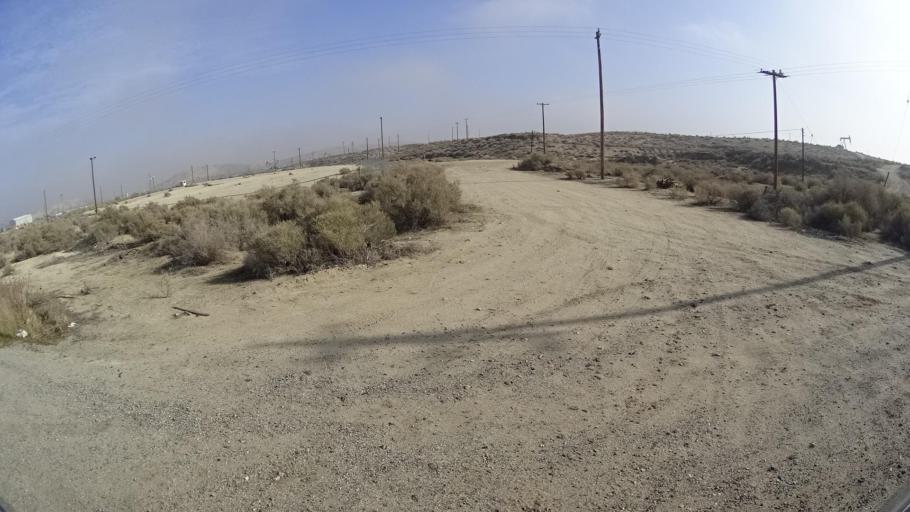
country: US
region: California
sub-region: Kern County
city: Ford City
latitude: 35.1746
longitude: -119.4654
